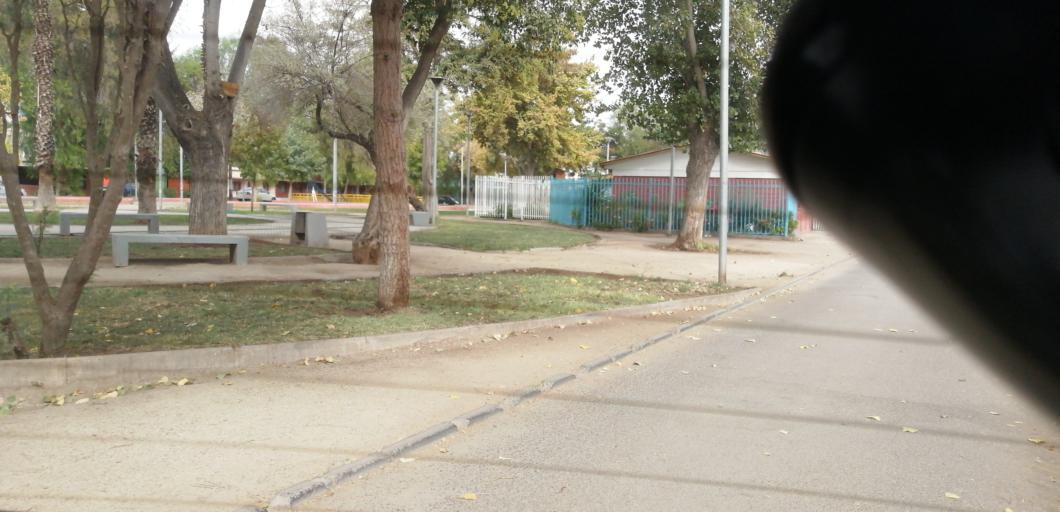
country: CL
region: Santiago Metropolitan
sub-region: Provincia de Santiago
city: Lo Prado
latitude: -33.4338
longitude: -70.7482
